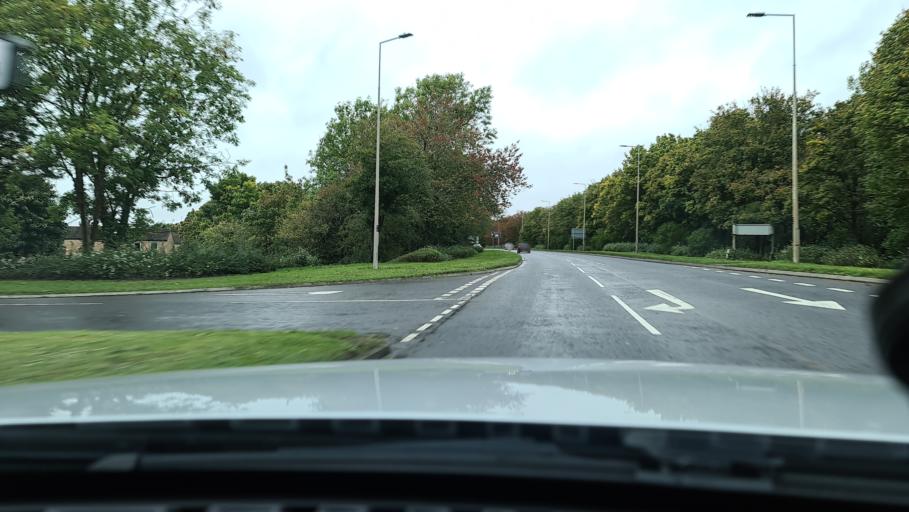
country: GB
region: England
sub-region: Milton Keynes
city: Bradwell
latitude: 52.0507
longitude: -0.8067
